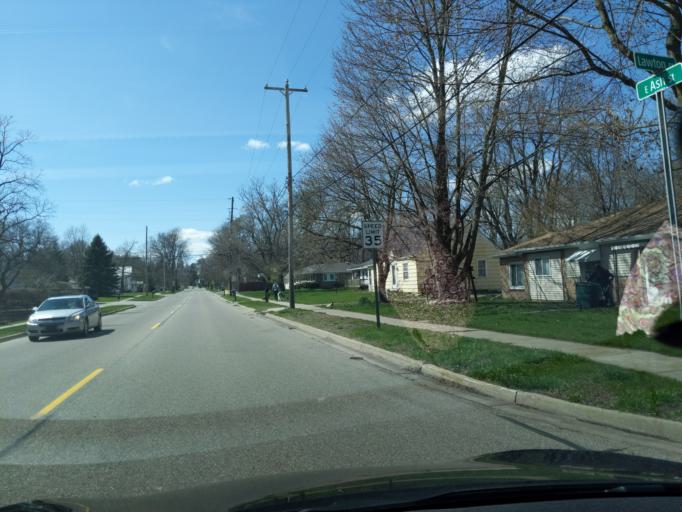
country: US
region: Michigan
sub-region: Ingham County
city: Mason
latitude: 42.5782
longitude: -84.4322
